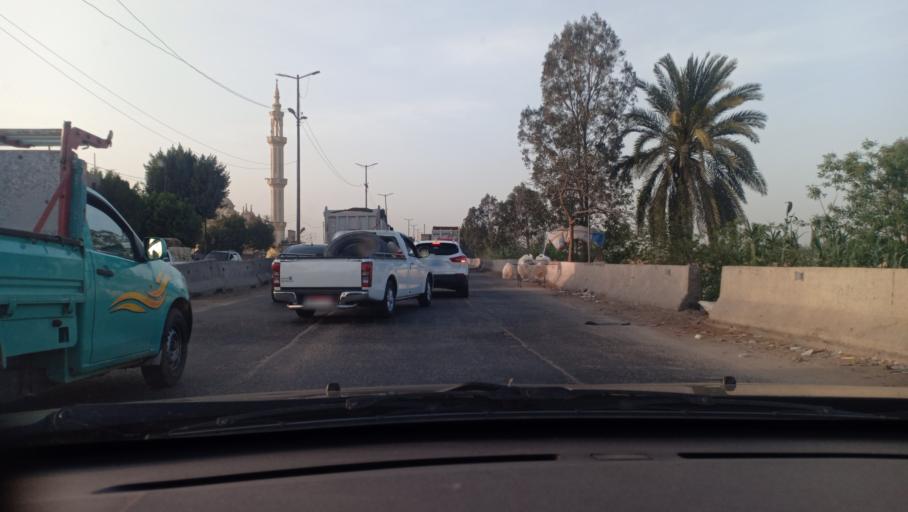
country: EG
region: Muhafazat al Minufiyah
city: Quwaysina
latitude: 30.5892
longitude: 31.2736
